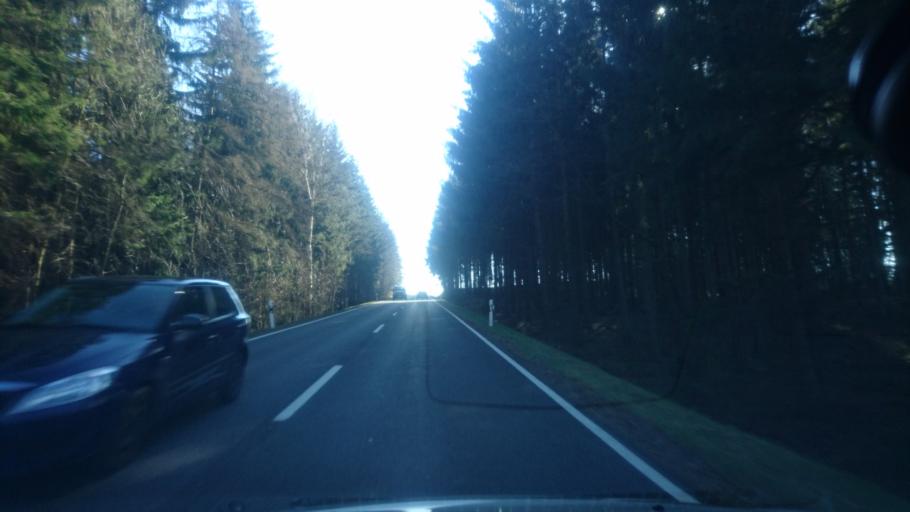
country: DE
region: Saxony
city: Neustadt Vogtland
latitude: 50.4770
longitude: 12.3253
